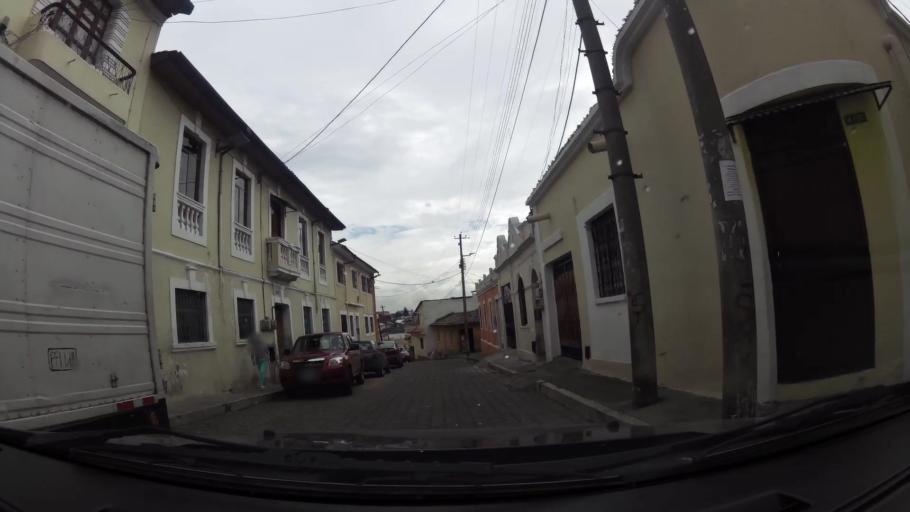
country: EC
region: Pichincha
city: Quito
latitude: -0.2284
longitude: -78.5083
